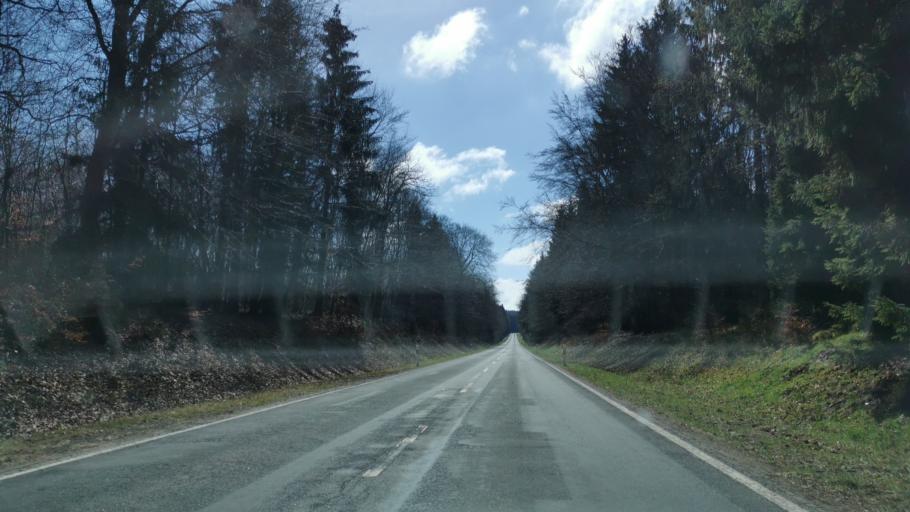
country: DE
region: Rheinland-Pfalz
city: Horath
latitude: 49.8425
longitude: 6.9835
